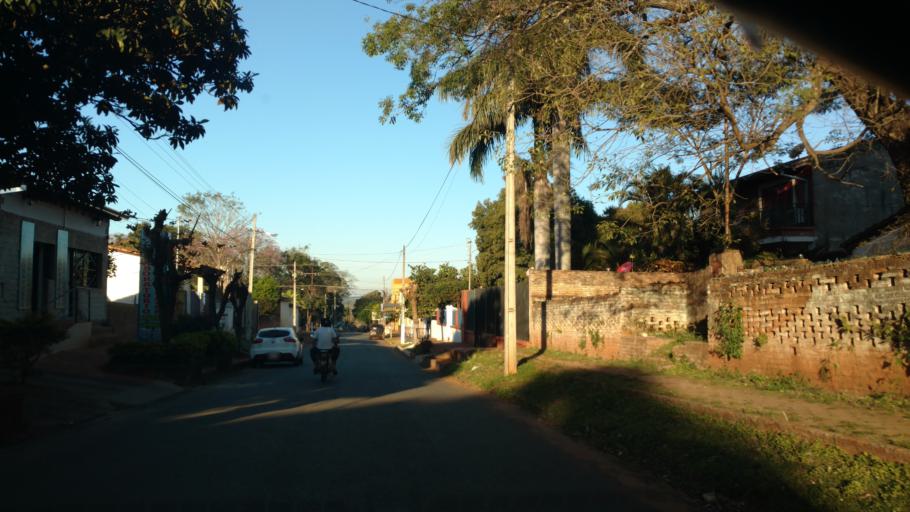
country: PY
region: Paraguari
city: Yaguaron
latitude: -25.5639
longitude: -57.2851
